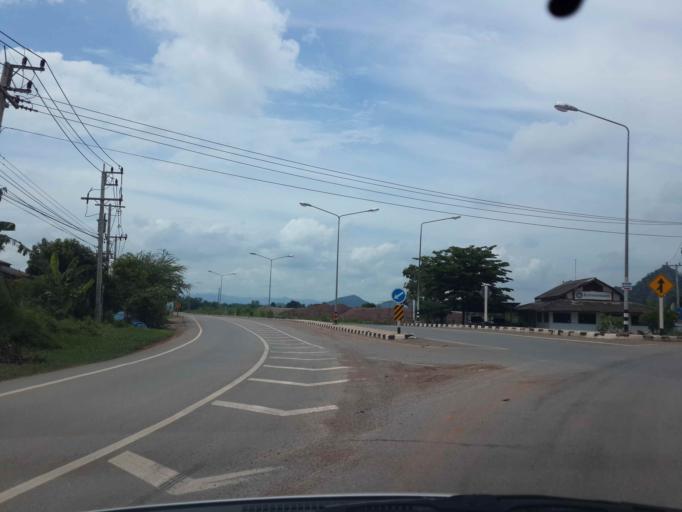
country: TH
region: Ratchaburi
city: Pak Tho
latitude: 13.3655
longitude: 99.7969
